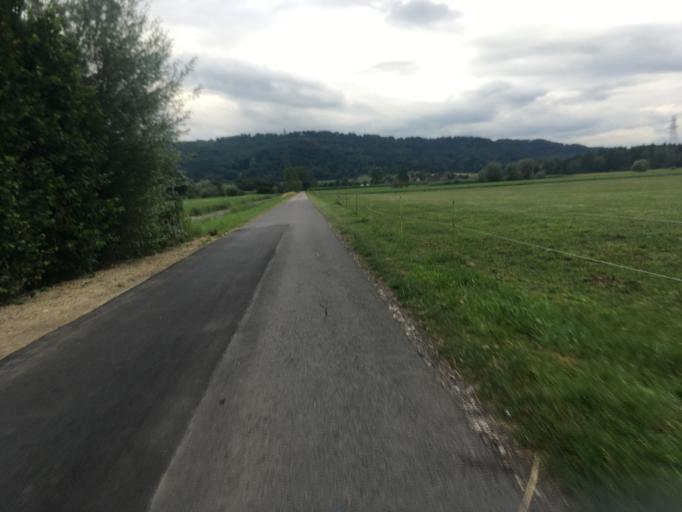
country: CH
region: Bern
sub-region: Seeland District
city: Ins
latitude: 46.9846
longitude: 7.1031
